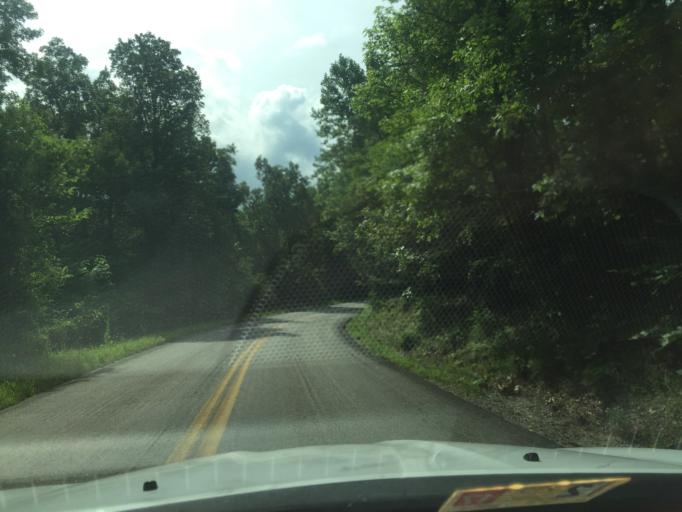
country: US
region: Virginia
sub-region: Charles City County
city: Charles City
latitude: 37.4097
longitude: -77.0284
